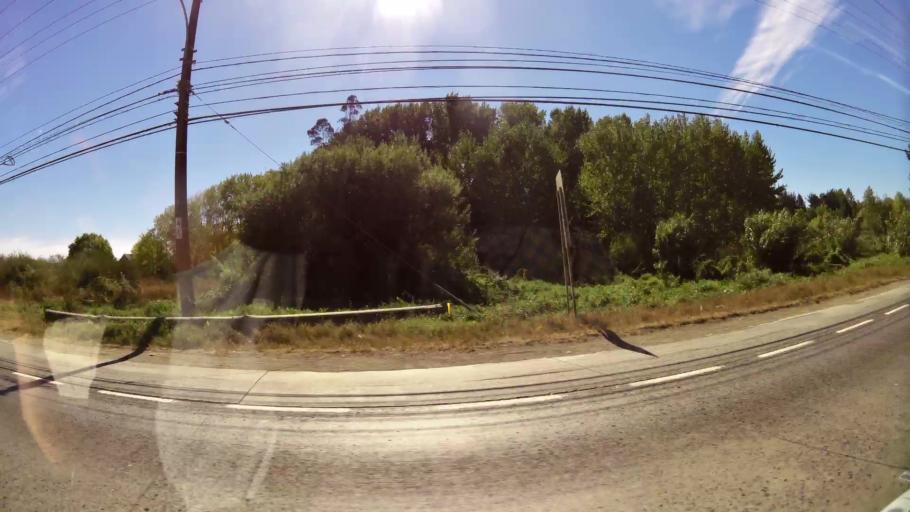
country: CL
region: Biobio
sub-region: Provincia de Concepcion
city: Penco
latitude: -36.7748
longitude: -73.0164
